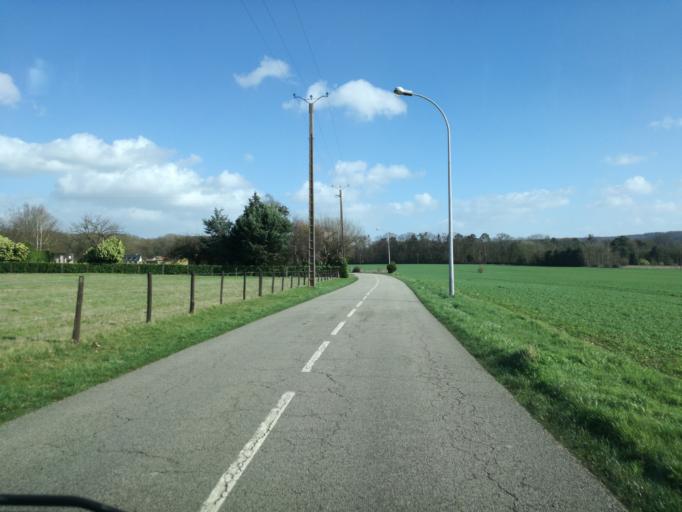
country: FR
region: Haute-Normandie
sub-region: Departement de la Seine-Maritime
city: Sahurs
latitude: 49.3574
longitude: 0.9504
